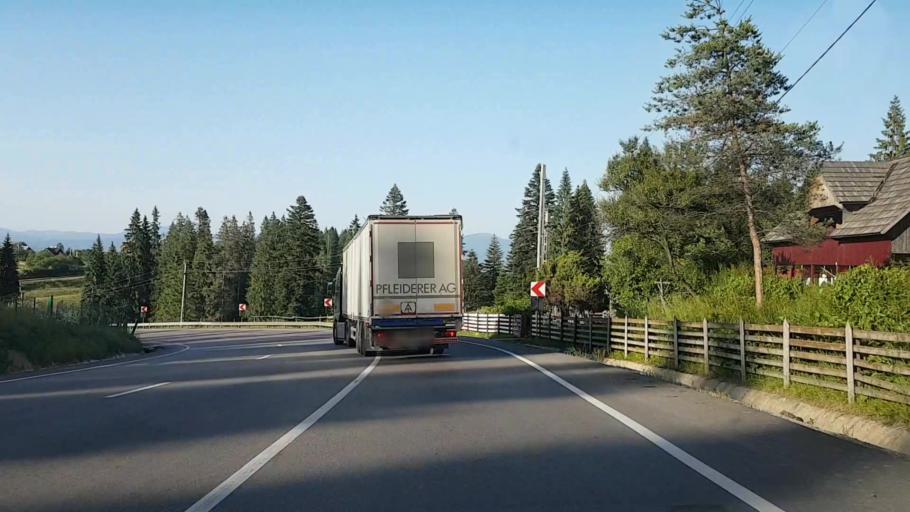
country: RO
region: Suceava
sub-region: Comuna Poiana Stampei
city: Poiana Stampei
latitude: 47.2891
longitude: 25.0763
